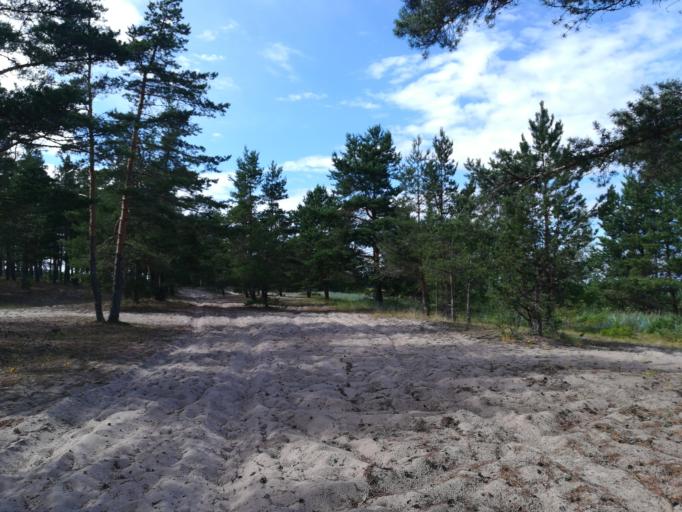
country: RU
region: Leningrad
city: Ust'-Luga
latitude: 59.6815
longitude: 28.2308
